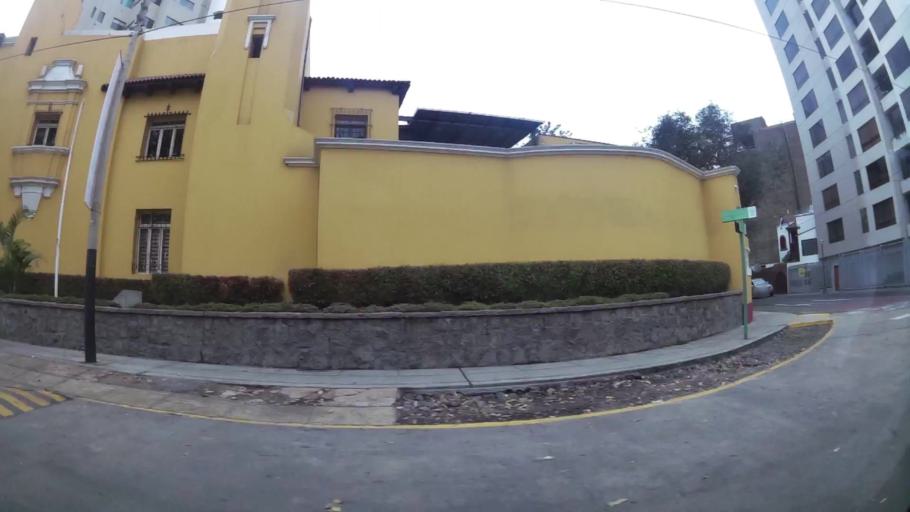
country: PE
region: Lima
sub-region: Lima
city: Surco
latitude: -12.1338
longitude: -77.0286
